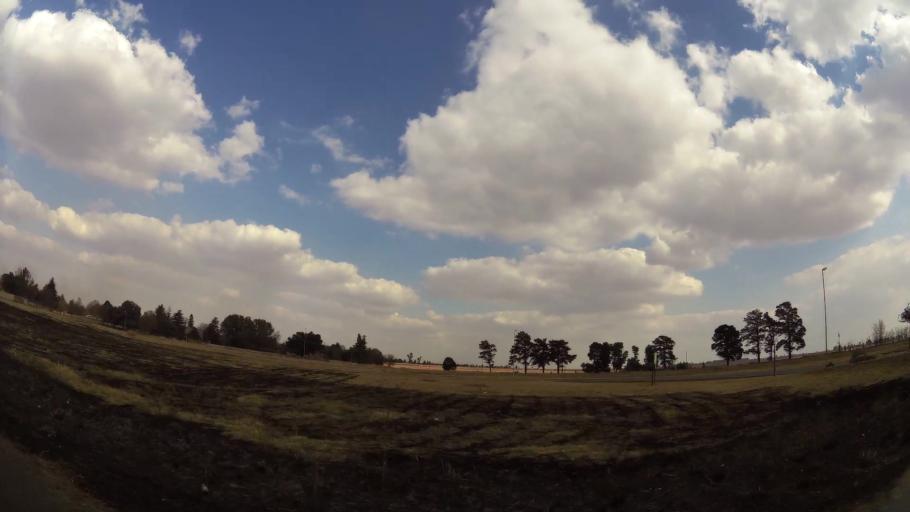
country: ZA
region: Mpumalanga
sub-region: Nkangala District Municipality
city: Delmas
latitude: -26.1396
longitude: 28.6662
